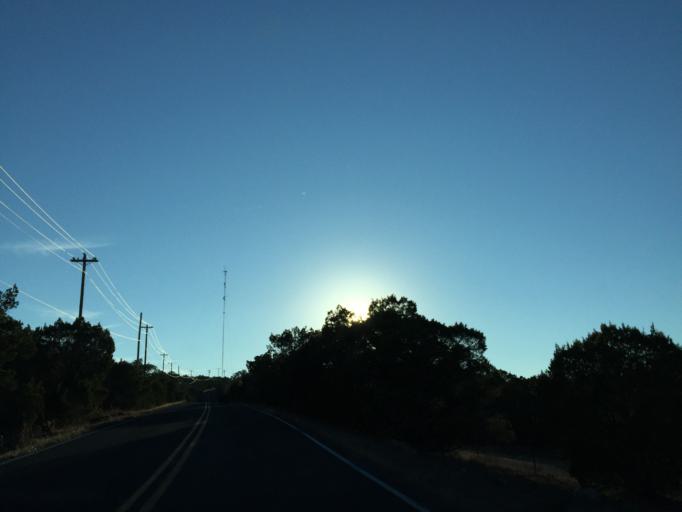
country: US
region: Texas
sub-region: Travis County
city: Lago Vista
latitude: 30.5076
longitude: -98.0475
